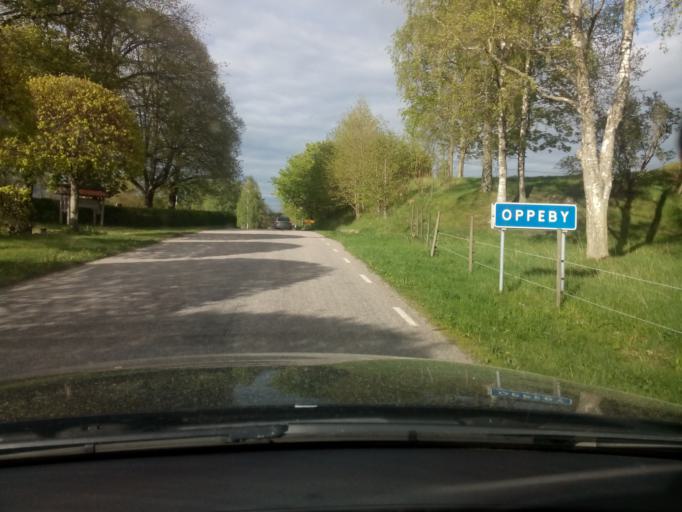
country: SE
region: Soedermanland
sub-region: Nykopings Kommun
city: Stigtomta
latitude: 58.9222
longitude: 16.8818
